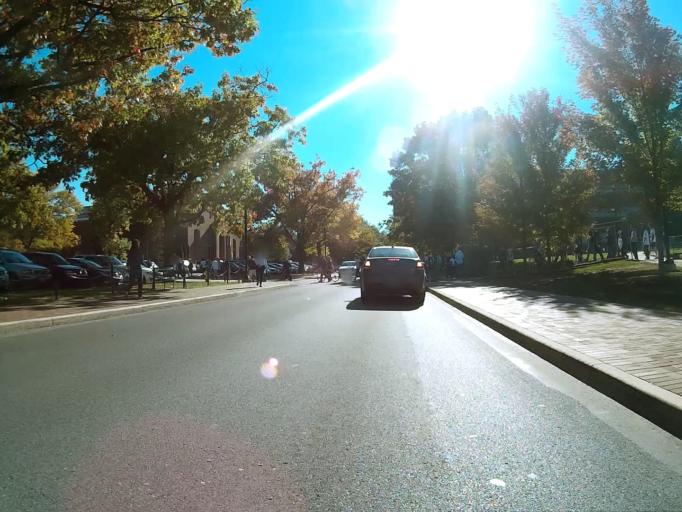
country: US
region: Pennsylvania
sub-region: Centre County
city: State College
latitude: 40.8019
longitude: -77.8583
